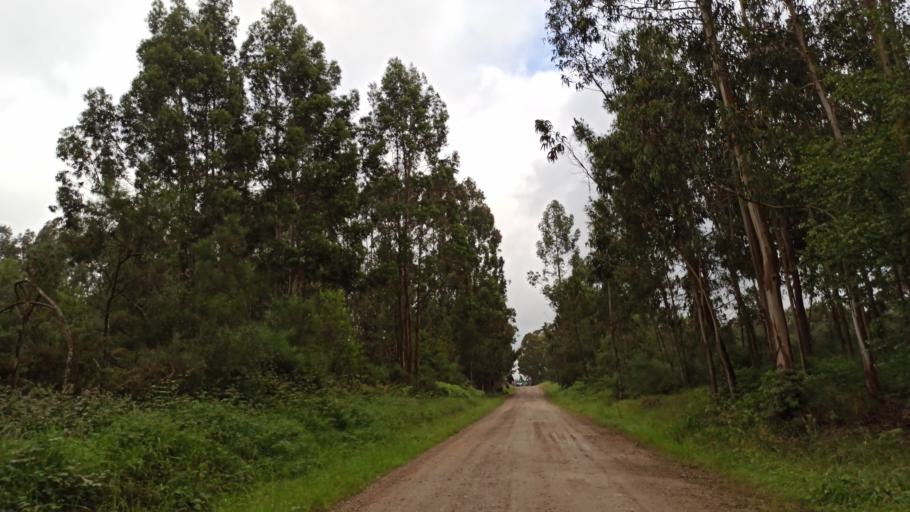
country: ES
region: Galicia
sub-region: Provincia da Coruna
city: Santiso
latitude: 42.7660
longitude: -8.0258
